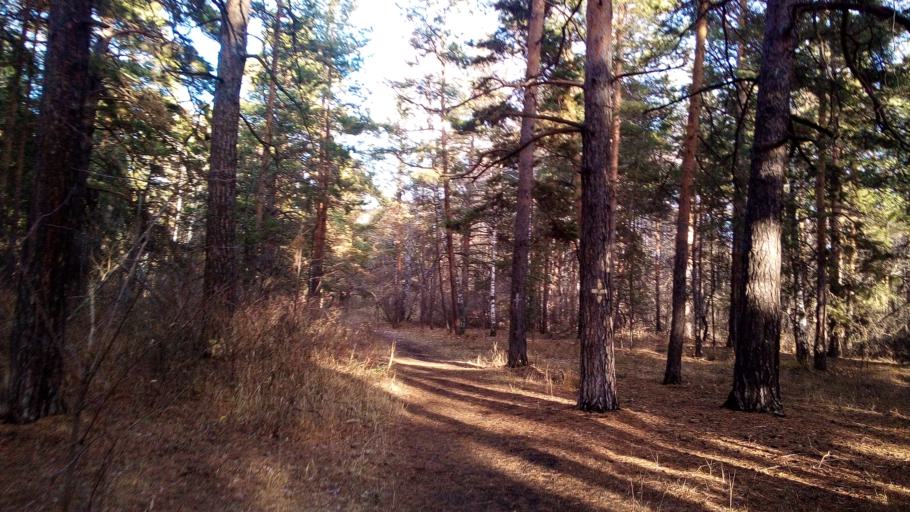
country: RU
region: Chelyabinsk
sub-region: Gorod Chelyabinsk
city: Chelyabinsk
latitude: 55.1572
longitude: 61.3529
